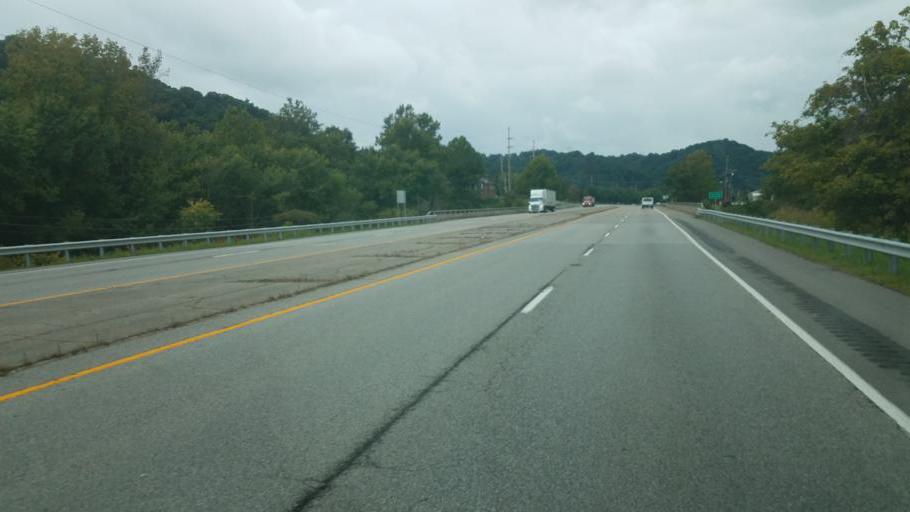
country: US
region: Kentucky
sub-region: Greenup County
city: South Shore
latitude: 38.7226
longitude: -82.9518
